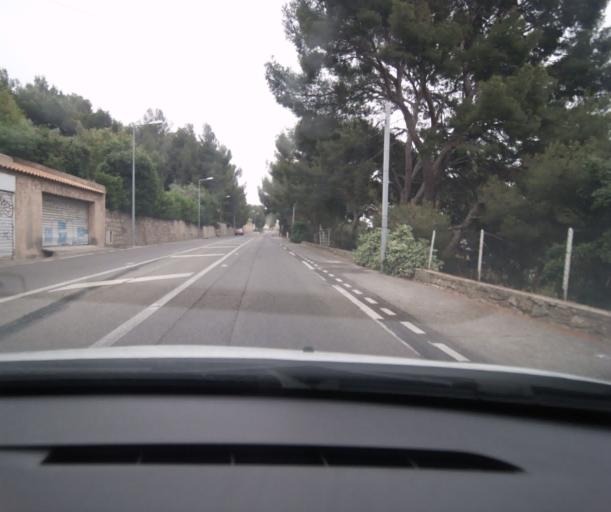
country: FR
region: Provence-Alpes-Cote d'Azur
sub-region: Departement du Var
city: Toulon
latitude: 43.1346
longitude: 5.9458
